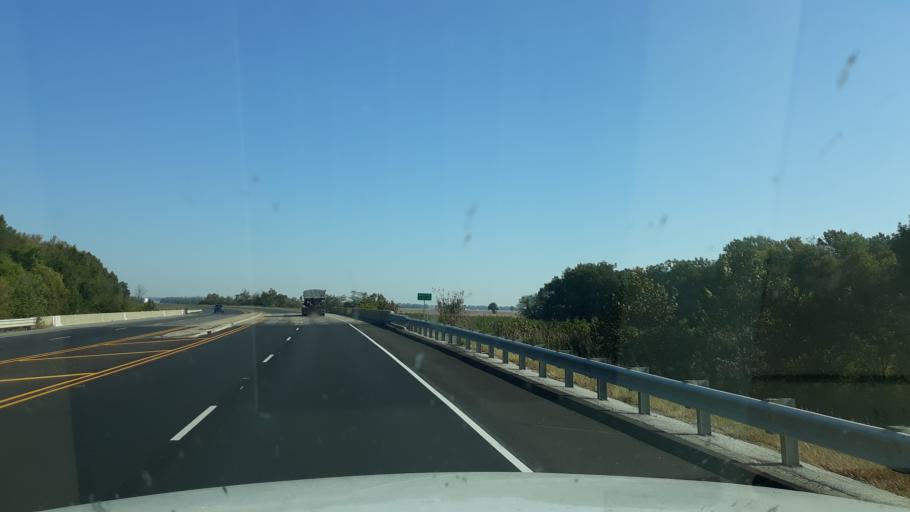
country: US
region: Illinois
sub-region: Saline County
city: Harrisburg
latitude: 37.7515
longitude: -88.5149
